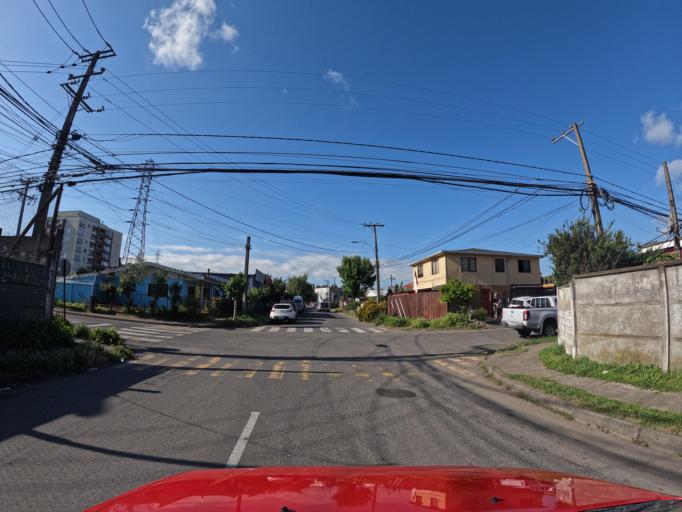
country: CL
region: Biobio
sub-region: Provincia de Concepcion
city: Concepcion
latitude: -36.8401
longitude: -73.0919
